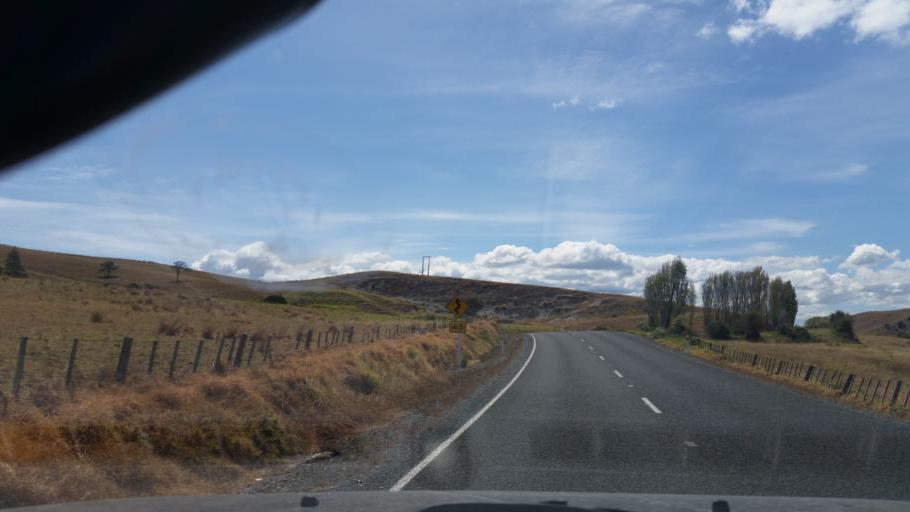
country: NZ
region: Northland
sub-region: Kaipara District
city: Dargaville
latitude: -36.1710
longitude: 174.1651
